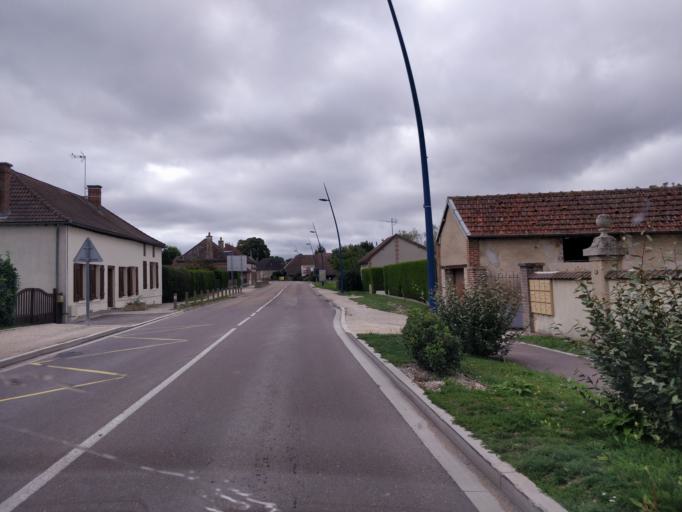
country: FR
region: Champagne-Ardenne
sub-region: Departement de l'Aube
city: Saint-Germain
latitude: 48.2613
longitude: 4.0342
